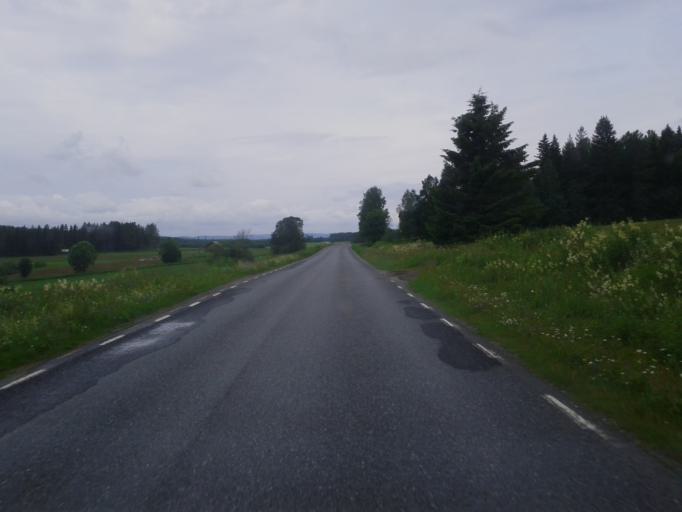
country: SE
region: Vaesterbotten
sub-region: Skelleftea Kommun
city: Viken
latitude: 64.8882
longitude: 20.7478
